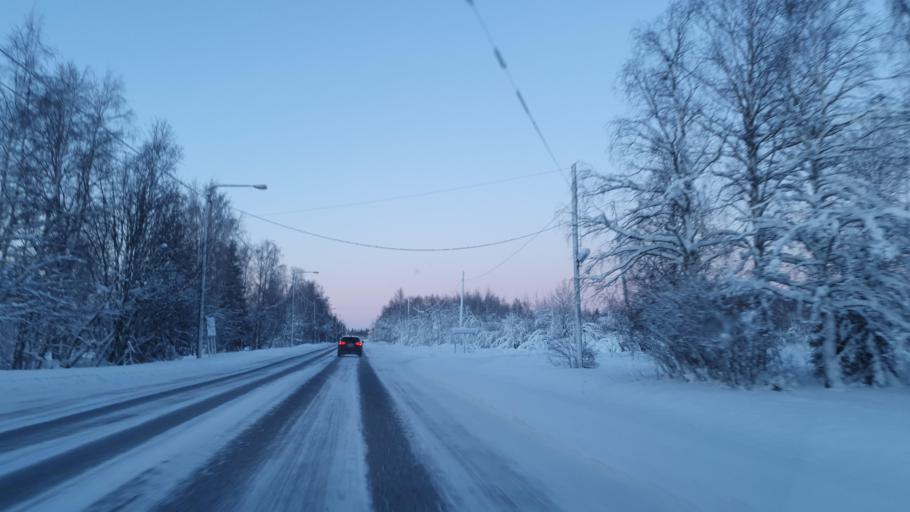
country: FI
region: Lapland
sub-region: Kemi-Tornio
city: Tornio
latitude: 66.0591
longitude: 23.9983
